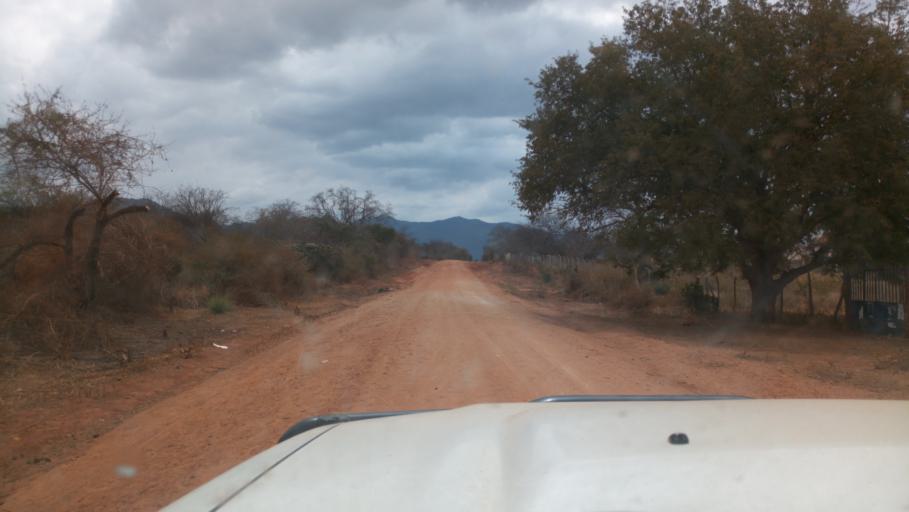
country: KE
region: Kitui
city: Kitui
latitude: -1.8548
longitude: 38.4232
